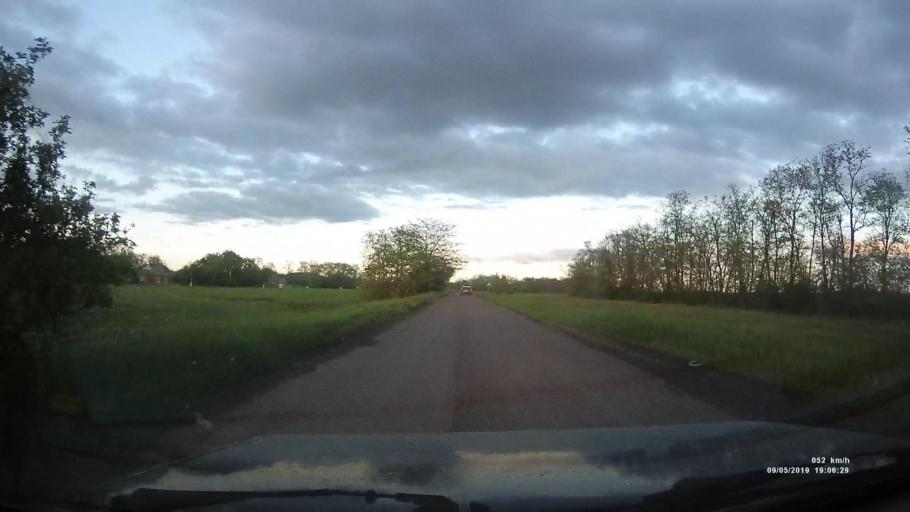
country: RU
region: Krasnodarskiy
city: Kanelovskaya
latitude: 46.7384
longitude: 39.1913
